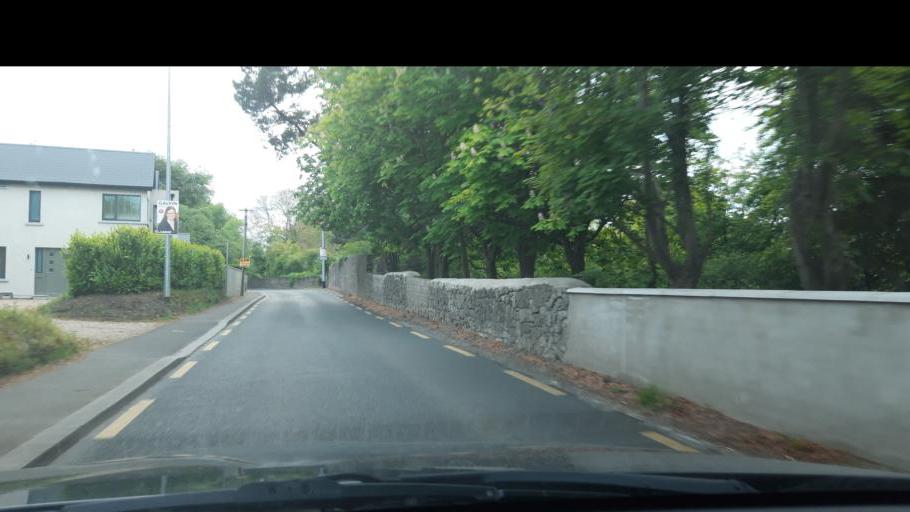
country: IE
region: Leinster
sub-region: Kildare
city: Celbridge
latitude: 53.3335
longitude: -6.5441
